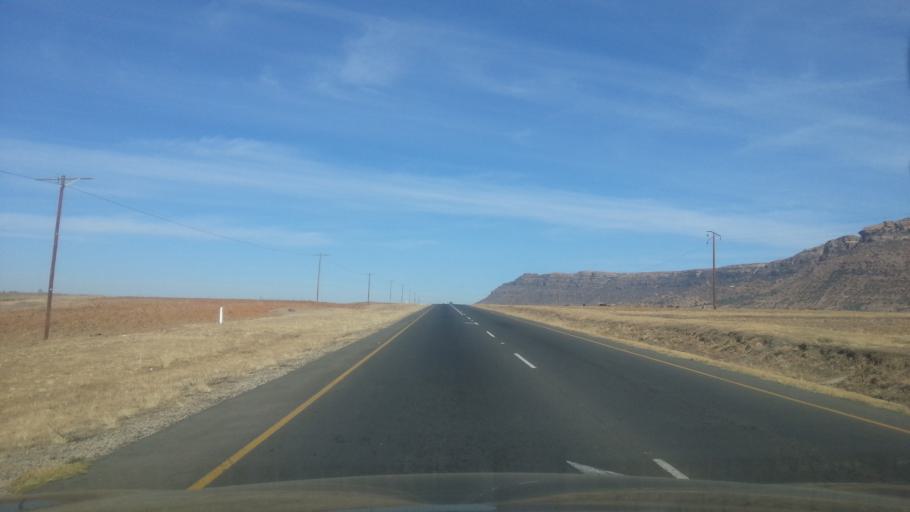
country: LS
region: Maseru
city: Maseru
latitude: -29.4712
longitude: 27.5332
